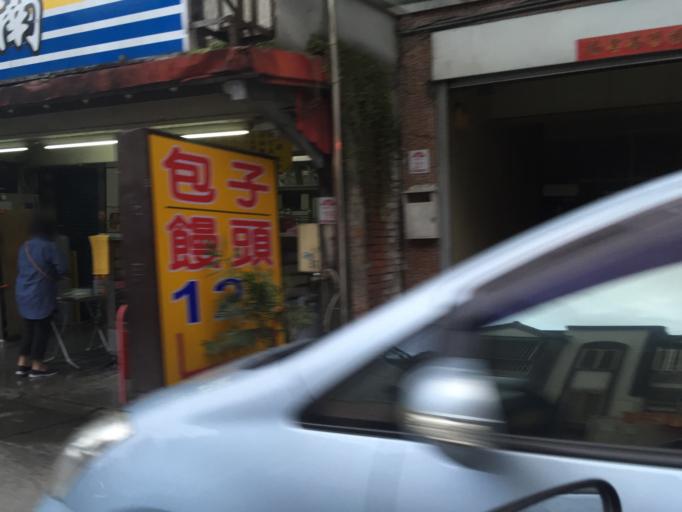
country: TW
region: Taiwan
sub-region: Yilan
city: Yilan
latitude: 24.7791
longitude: 121.7412
